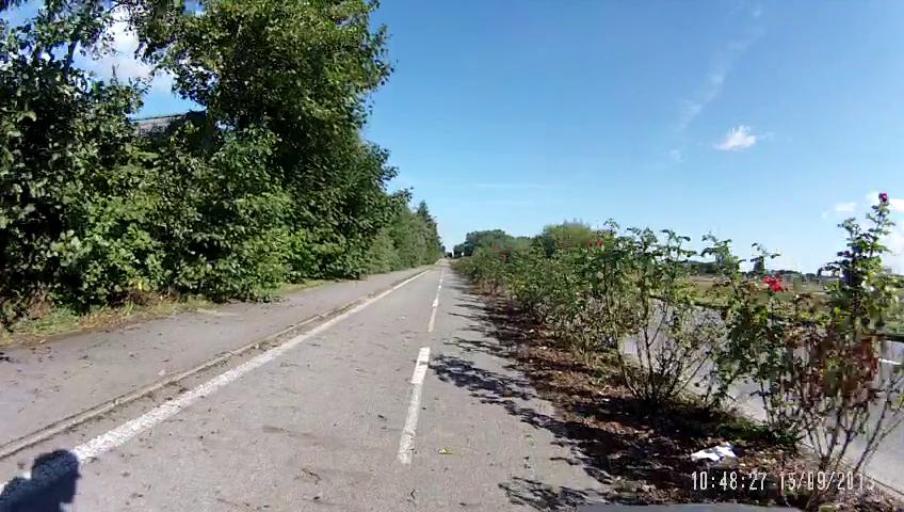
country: FR
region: Nord-Pas-de-Calais
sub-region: Departement du Nord
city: Leffrinckoucke
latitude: 51.0492
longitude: 2.4448
